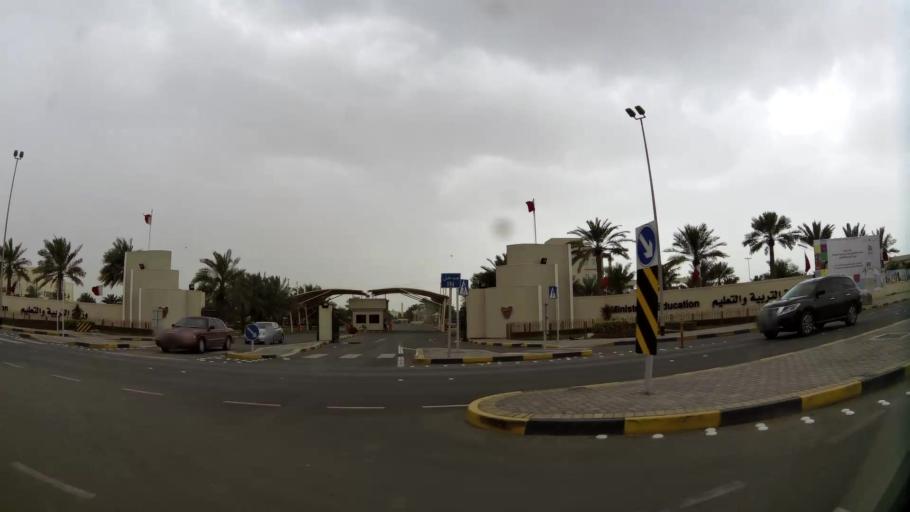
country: BH
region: Northern
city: Madinat `Isa
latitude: 26.1648
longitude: 50.5517
